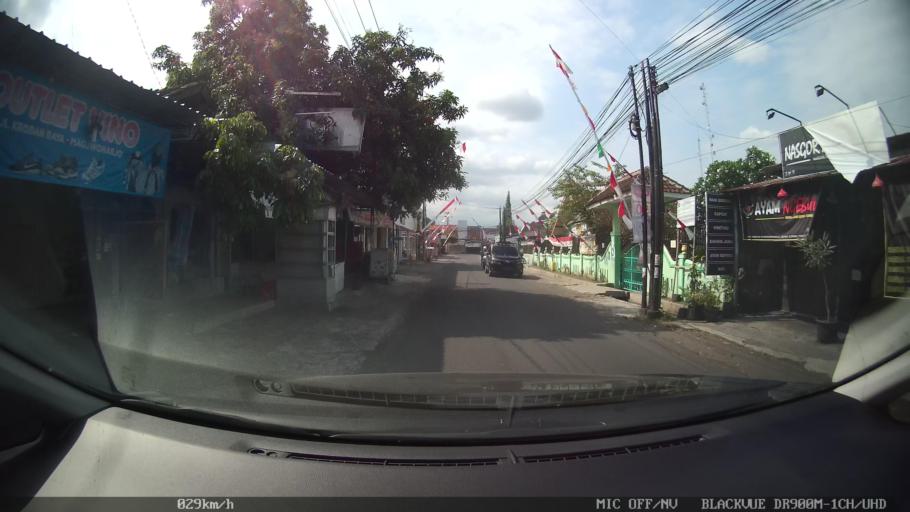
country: ID
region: Daerah Istimewa Yogyakarta
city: Depok
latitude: -7.7571
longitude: 110.4229
